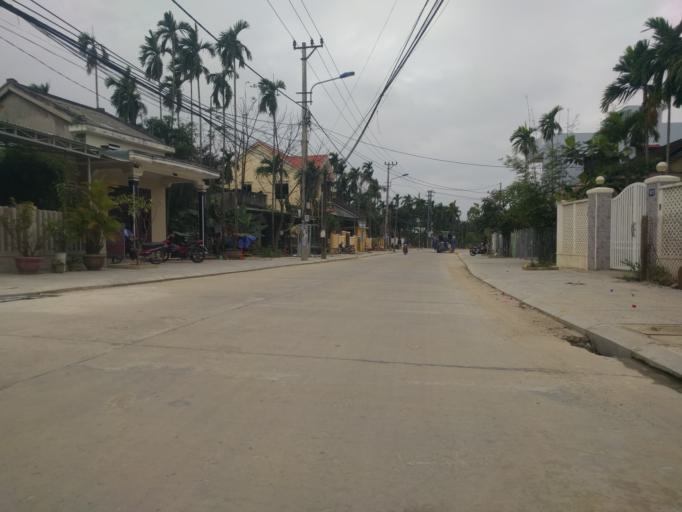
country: VN
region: Quang Nam
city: Hoi An
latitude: 15.8698
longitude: 108.3484
